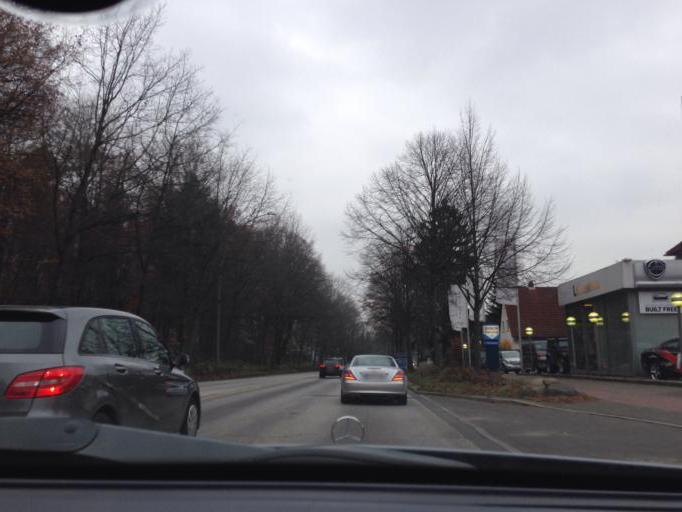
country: DE
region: Hamburg
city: Wellingsbuettel
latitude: 53.6394
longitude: 10.0952
